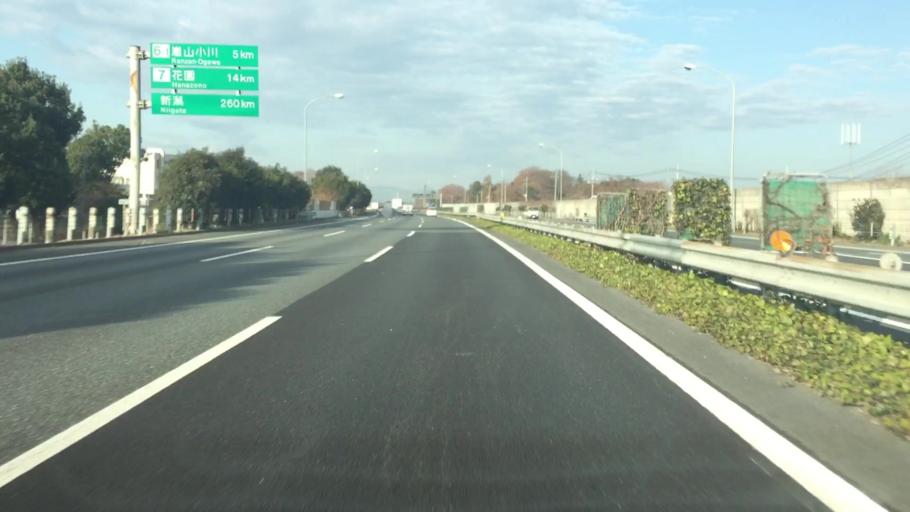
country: JP
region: Saitama
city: Sakado
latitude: 36.0435
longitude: 139.3629
